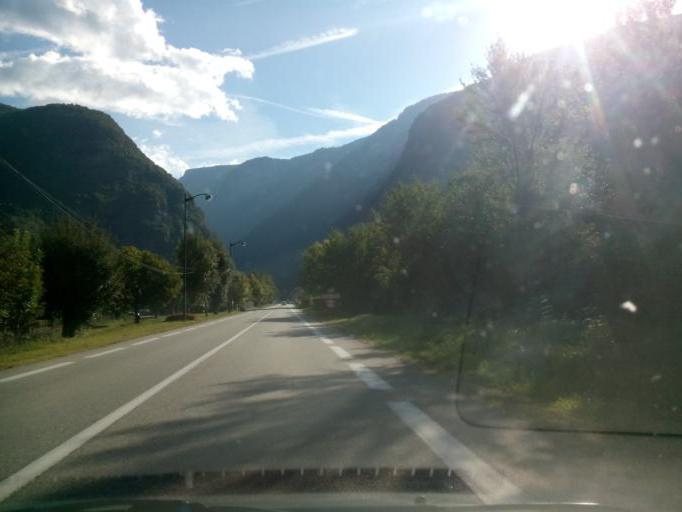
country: FR
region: Rhone-Alpes
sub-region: Departement de l'Isere
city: Vaulnaveys-le-Bas
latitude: 45.0532
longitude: 5.8258
